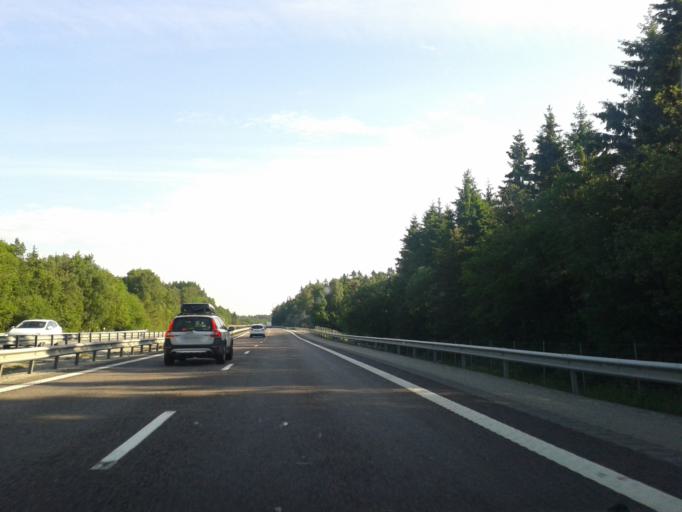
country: SE
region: Vaestra Goetaland
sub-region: Stenungsunds Kommun
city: Stora Hoga
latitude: 57.9874
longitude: 11.8424
